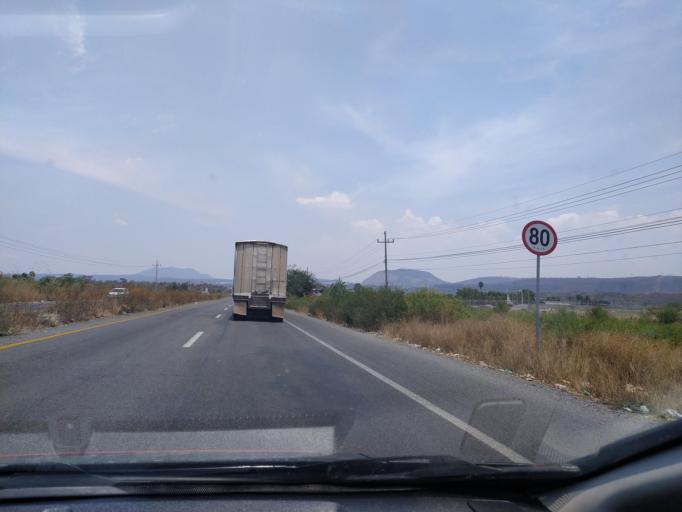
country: MX
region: Jalisco
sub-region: Acatlan de Juarez
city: Villa de los Ninos
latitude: 20.3962
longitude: -103.5935
